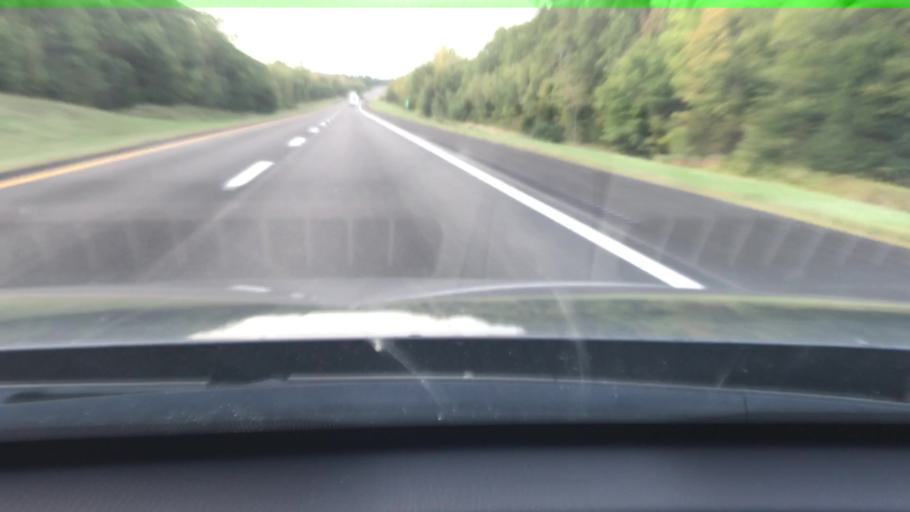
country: US
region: Maine
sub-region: Sagadahoc County
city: Richmond
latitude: 44.0810
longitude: -69.8778
